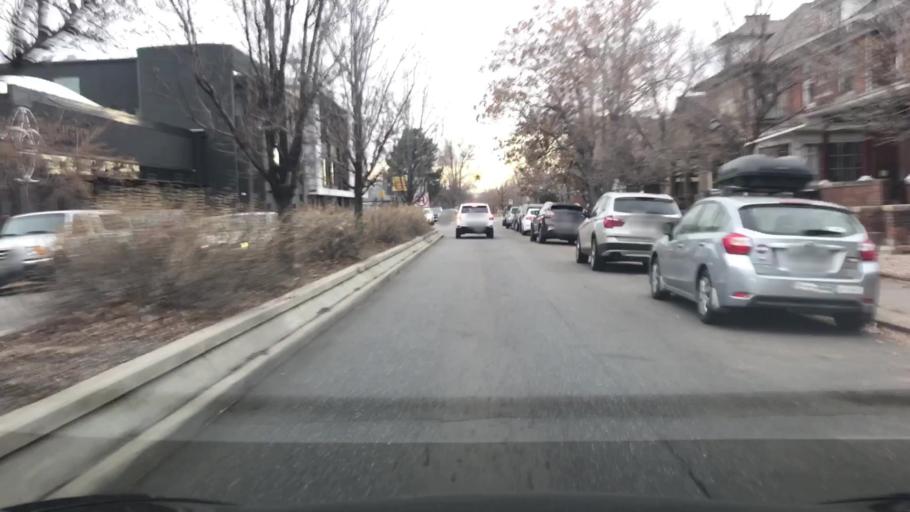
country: US
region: Colorado
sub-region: Denver County
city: Denver
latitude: 39.7157
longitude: -104.9827
